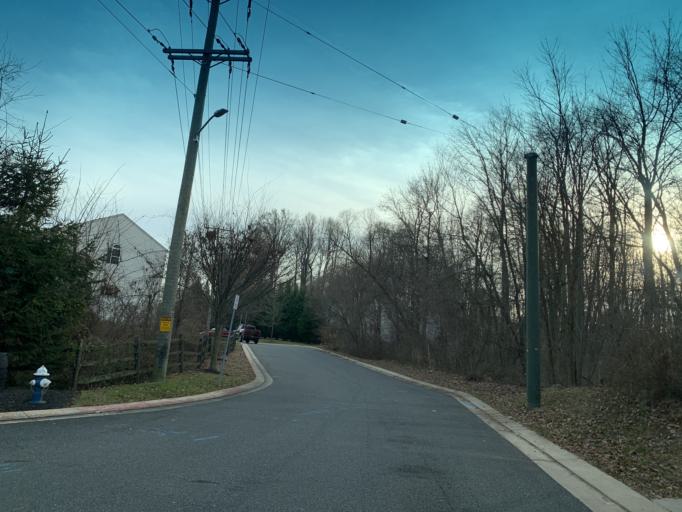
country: US
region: Maryland
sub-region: Harford County
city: North Bel Air
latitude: 39.5452
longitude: -76.3557
